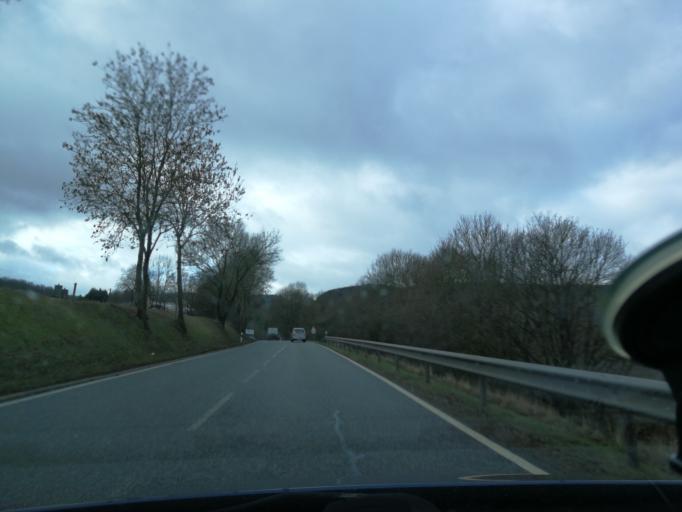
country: DE
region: Rheinland-Pfalz
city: Oberehe-Stroheich
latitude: 50.2791
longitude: 6.7670
